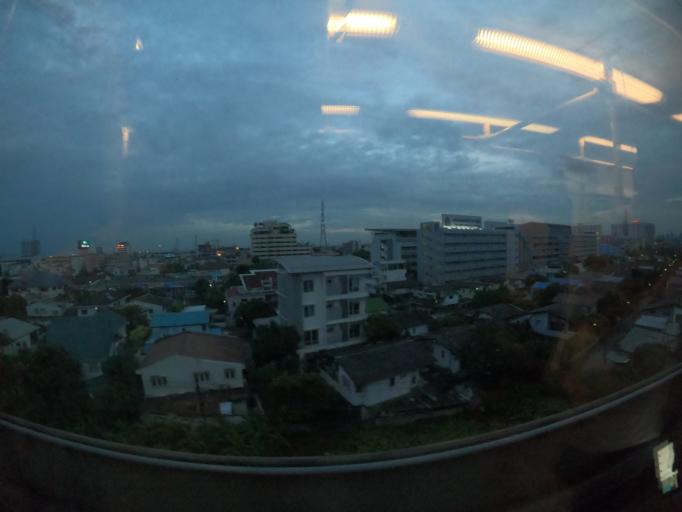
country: TH
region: Bangkok
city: Suan Luang
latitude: 13.7394
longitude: 100.6303
